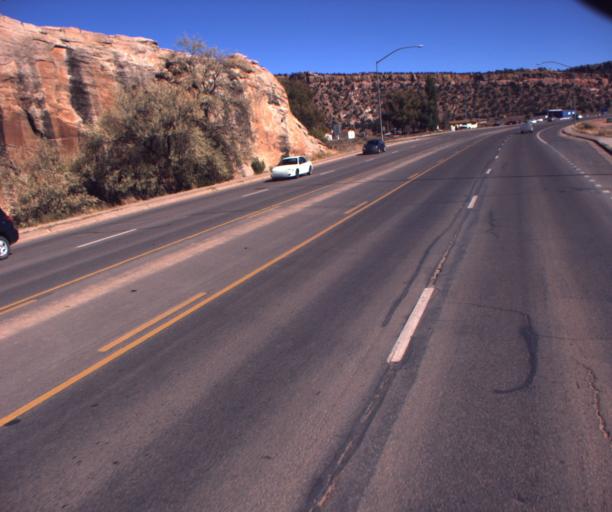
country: US
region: Arizona
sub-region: Apache County
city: Window Rock
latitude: 35.6631
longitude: -109.0501
